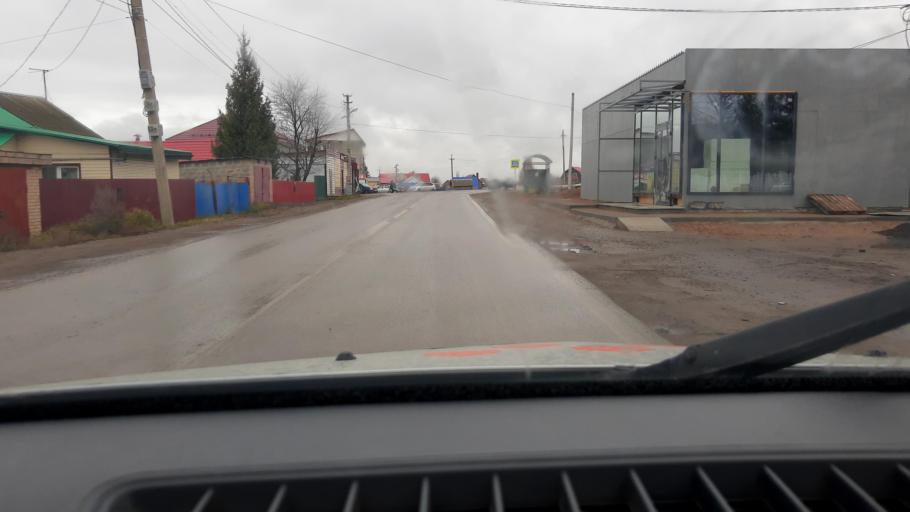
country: RU
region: Bashkortostan
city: Iglino
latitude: 54.7901
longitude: 56.2349
